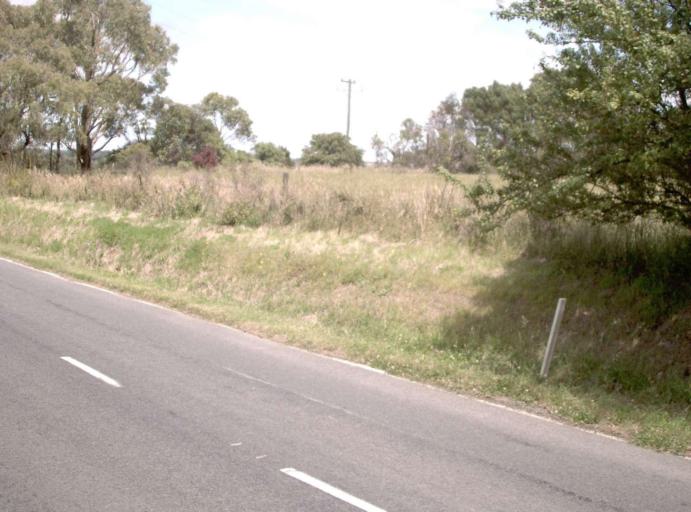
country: AU
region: Victoria
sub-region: Bass Coast
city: North Wonthaggi
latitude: -38.6103
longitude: 146.0171
